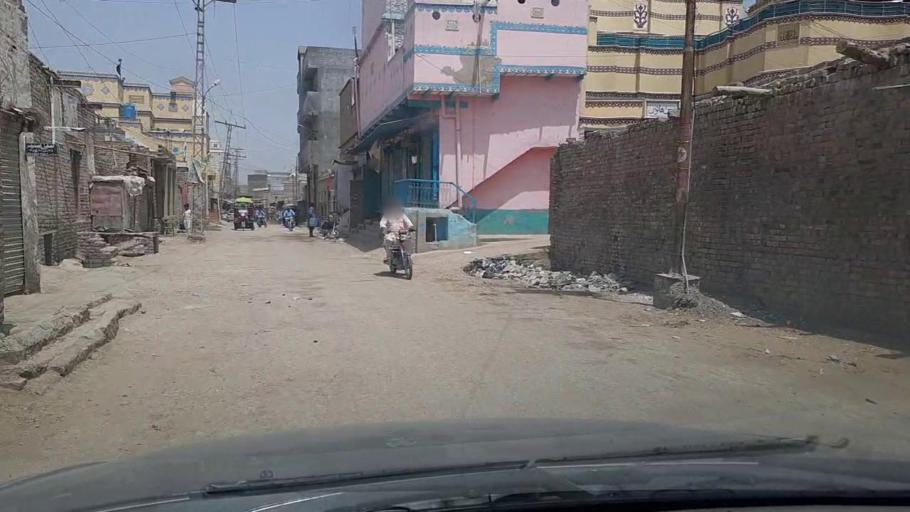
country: PK
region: Sindh
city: Ratodero
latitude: 27.8008
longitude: 68.2871
